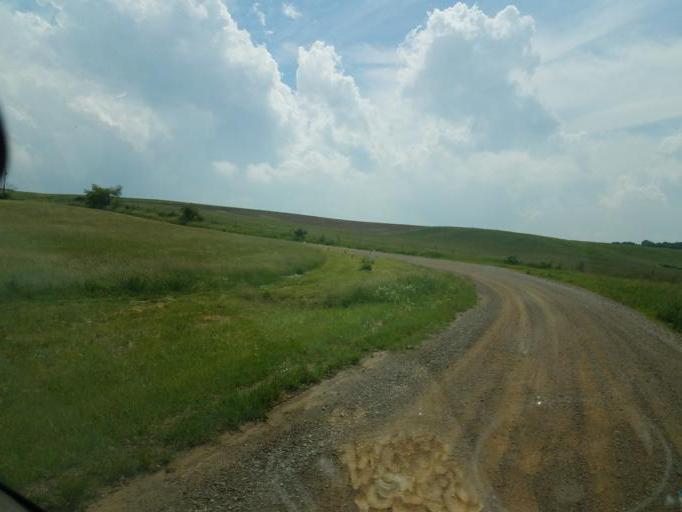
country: US
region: Ohio
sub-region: Knox County
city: Oak Hill
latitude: 40.2910
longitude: -82.2682
